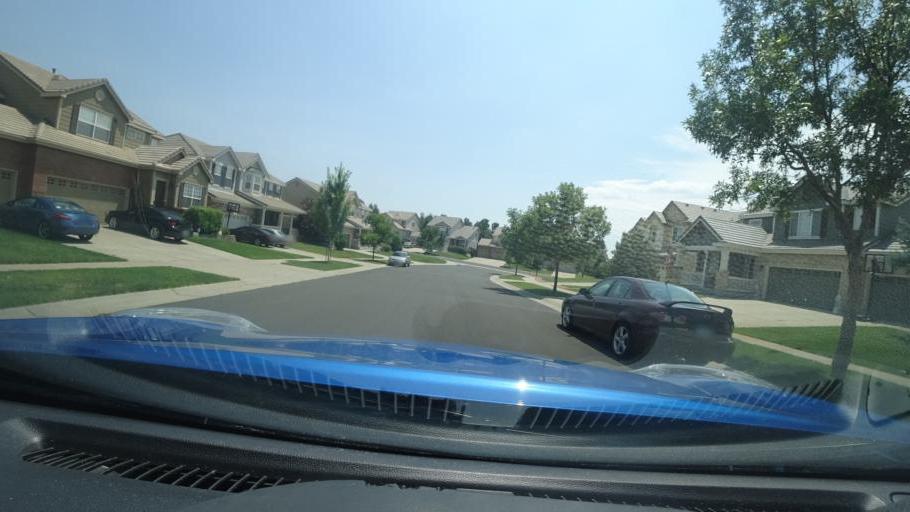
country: US
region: Colorado
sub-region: Adams County
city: Aurora
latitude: 39.6738
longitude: -104.7667
